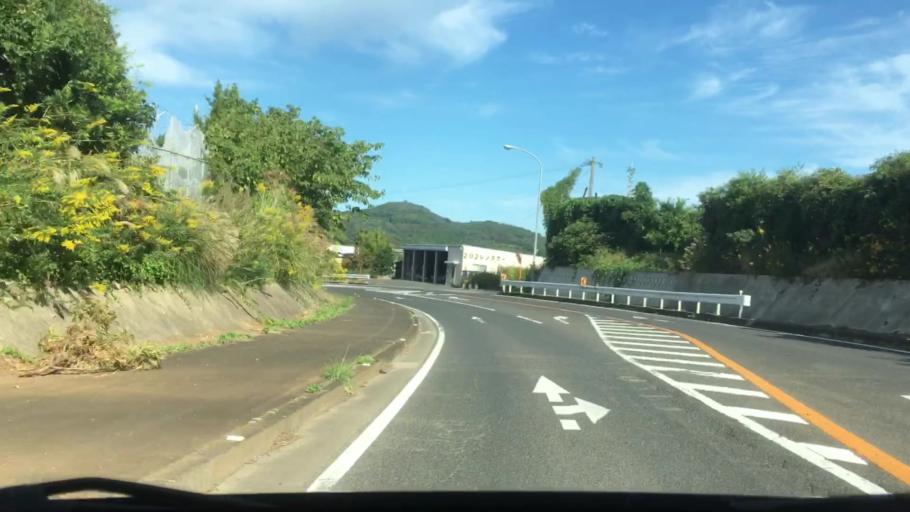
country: JP
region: Nagasaki
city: Sasebo
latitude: 33.0755
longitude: 129.7596
